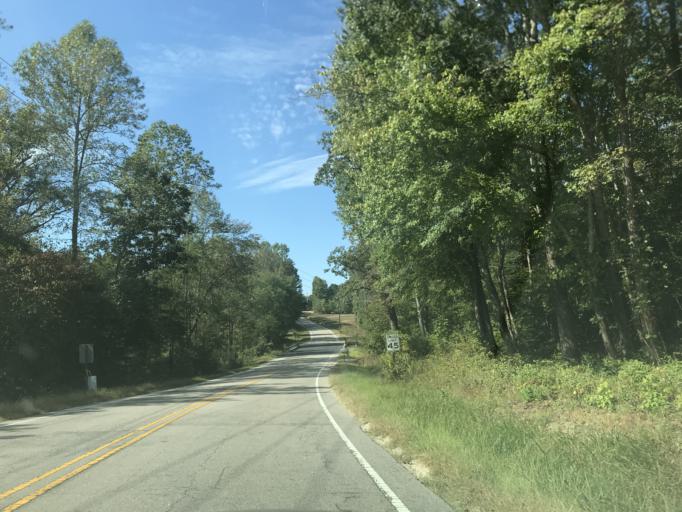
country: US
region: North Carolina
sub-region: Wake County
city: Rolesville
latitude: 35.8790
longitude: -78.4911
